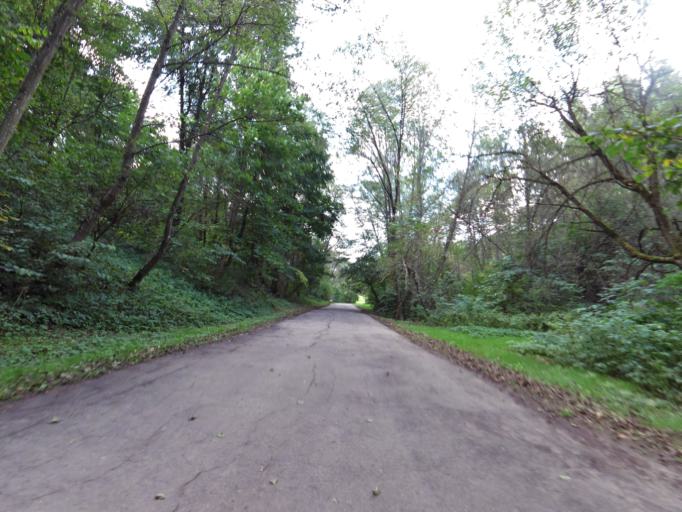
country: LT
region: Vilnius County
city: Seskine
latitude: 54.7056
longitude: 25.2486
